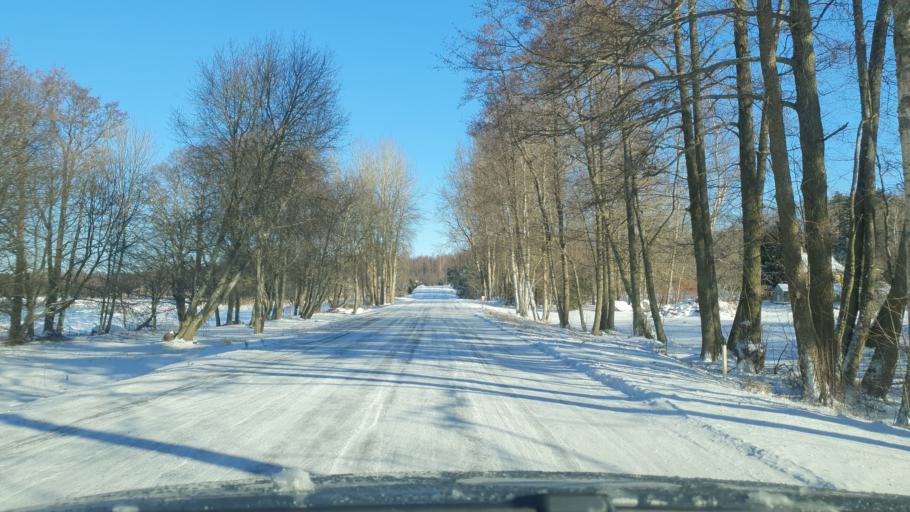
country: EE
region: Harju
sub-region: Kuusalu vald
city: Kuusalu
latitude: 59.5962
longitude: 25.5026
